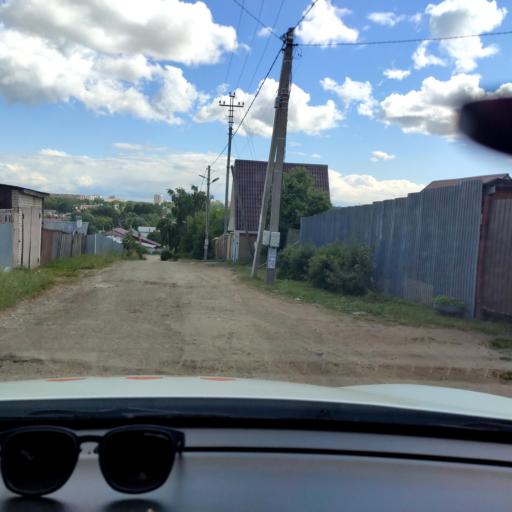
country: RU
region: Tatarstan
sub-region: Gorod Kazan'
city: Kazan
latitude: 55.8843
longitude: 49.0804
